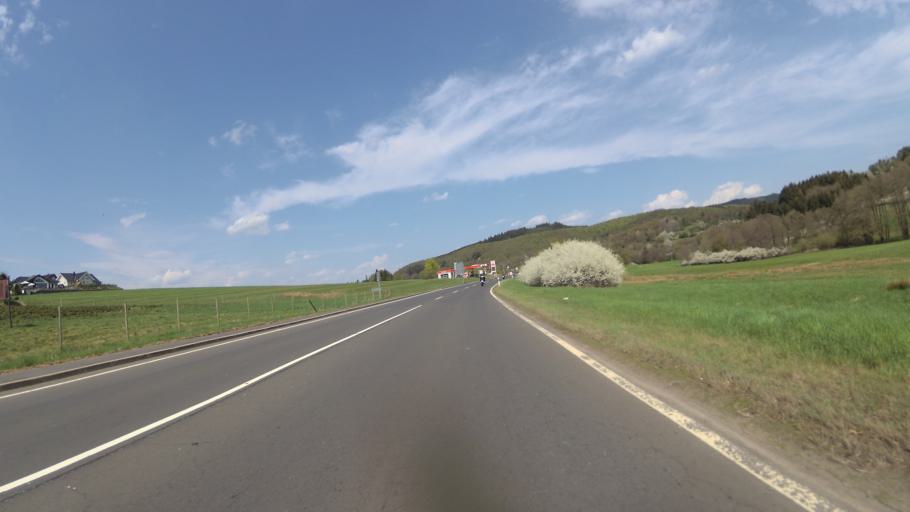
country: DE
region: Rheinland-Pfalz
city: Kelberg
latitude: 50.2918
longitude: 6.9211
